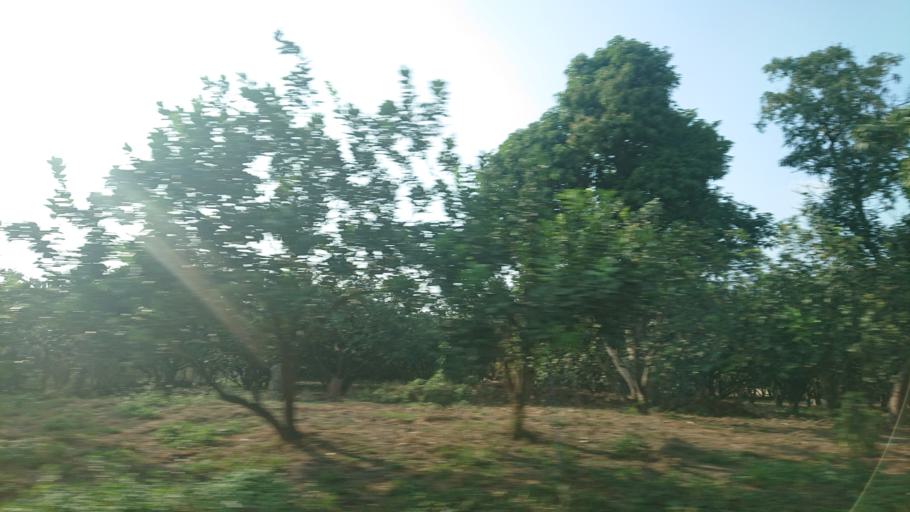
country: TW
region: Taiwan
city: Xinying
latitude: 23.1635
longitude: 120.2512
